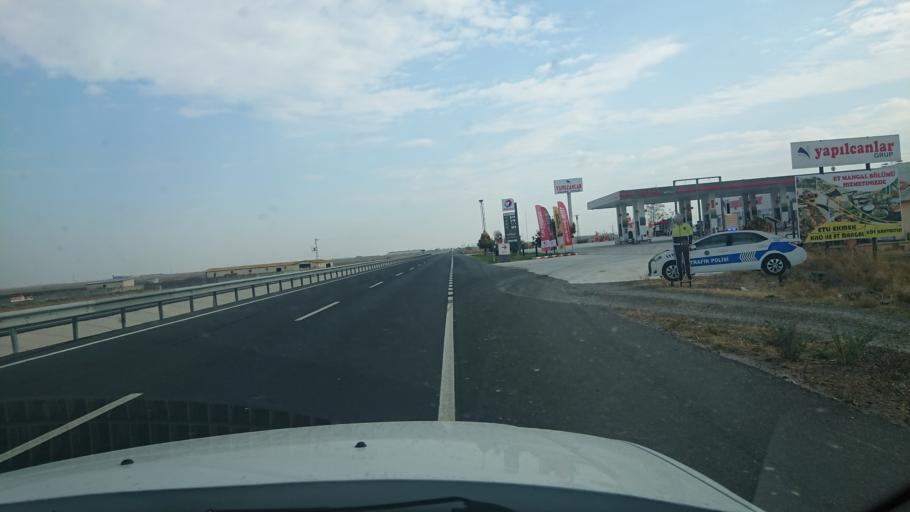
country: TR
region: Aksaray
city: Yesilova
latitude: 38.3026
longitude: 33.8038
